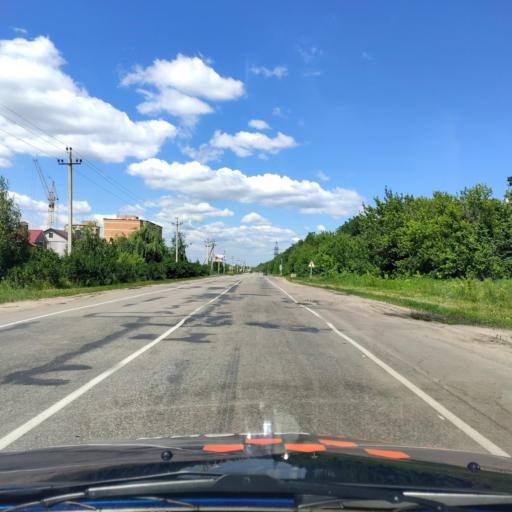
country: RU
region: Voronezj
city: Novaya Usman'
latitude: 51.6257
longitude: 39.3345
